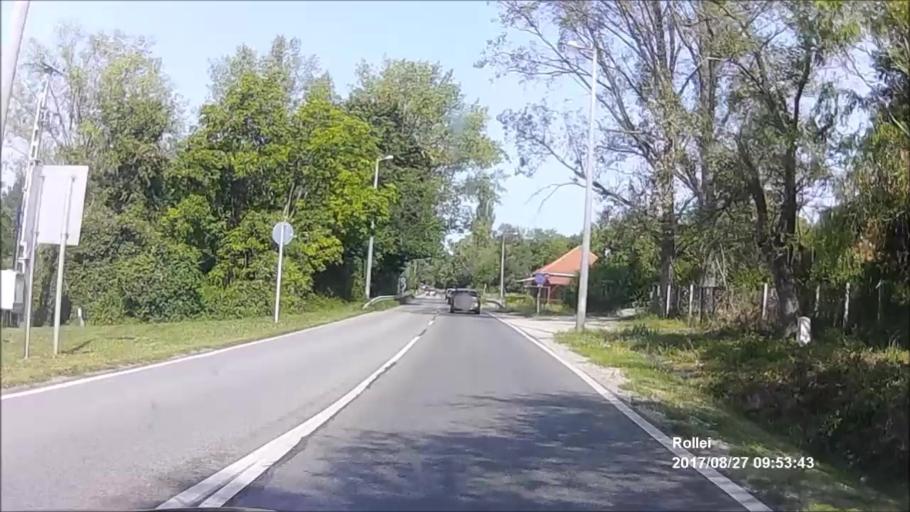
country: HU
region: Gyor-Moson-Sopron
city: Sopron
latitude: 47.7162
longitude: 16.5703
